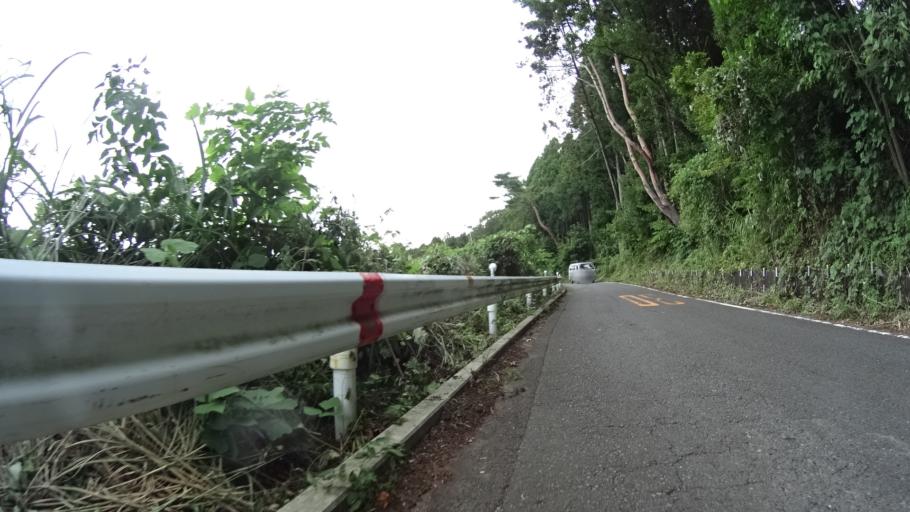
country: JP
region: Kanagawa
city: Hadano
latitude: 35.4116
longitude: 139.2183
